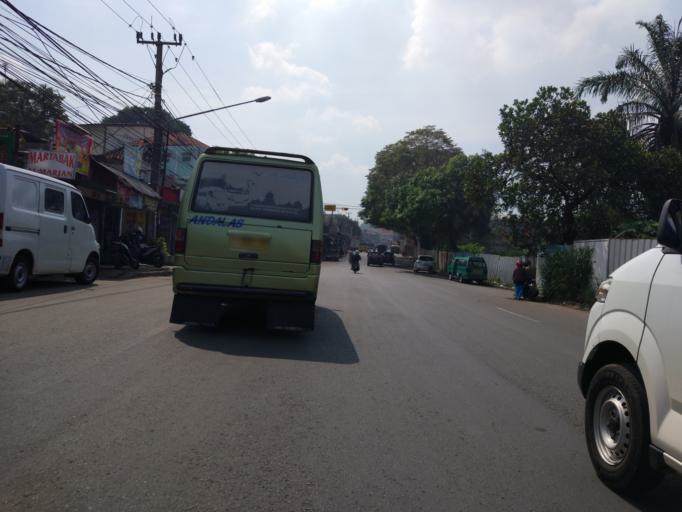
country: ID
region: West Java
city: Cileunyi
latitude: -6.9393
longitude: 107.7526
